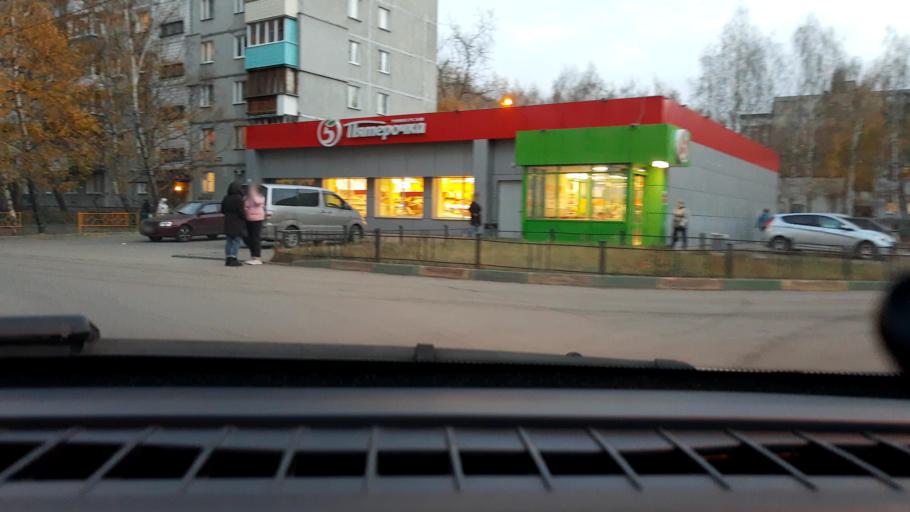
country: RU
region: Nizjnij Novgorod
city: Gorbatovka
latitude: 56.3639
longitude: 43.8044
